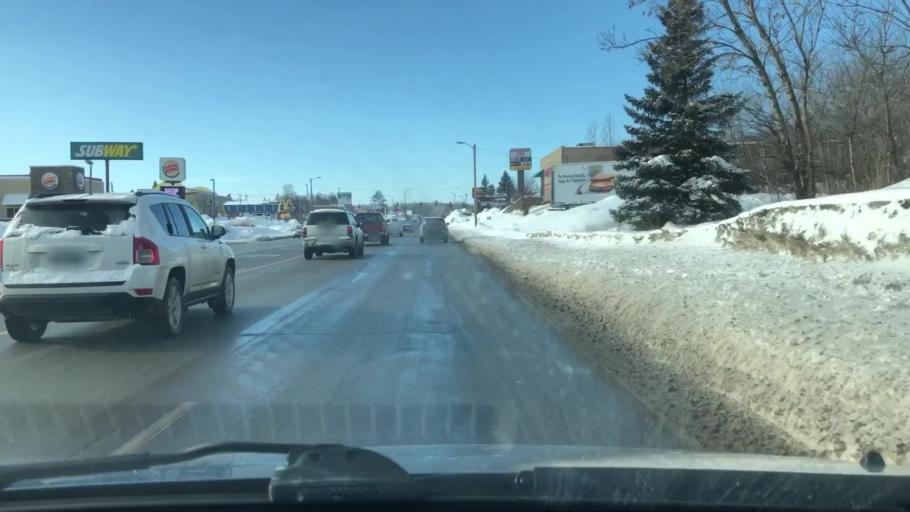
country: US
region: Minnesota
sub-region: Saint Louis County
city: Duluth
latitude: 46.8005
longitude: -92.1275
